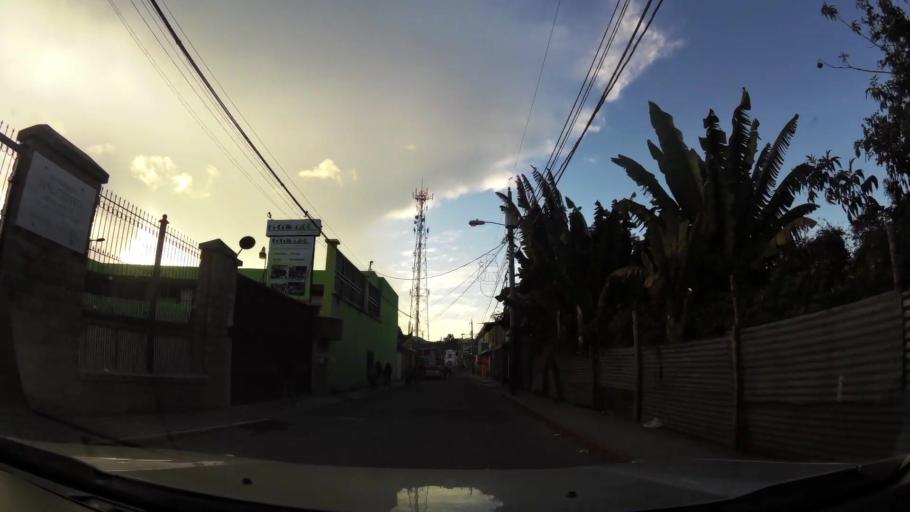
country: GT
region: Sacatepequez
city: San Lucas Sacatepequez
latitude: 14.6106
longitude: -90.6595
